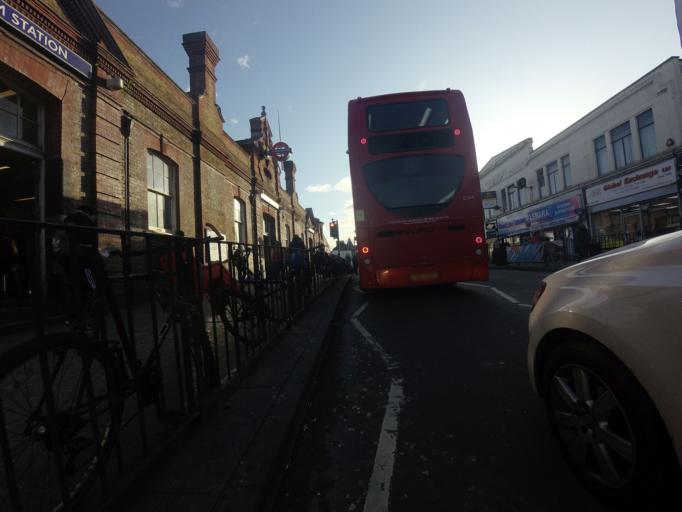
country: GB
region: England
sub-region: Greater London
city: East Ham
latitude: 51.5392
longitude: 0.0513
